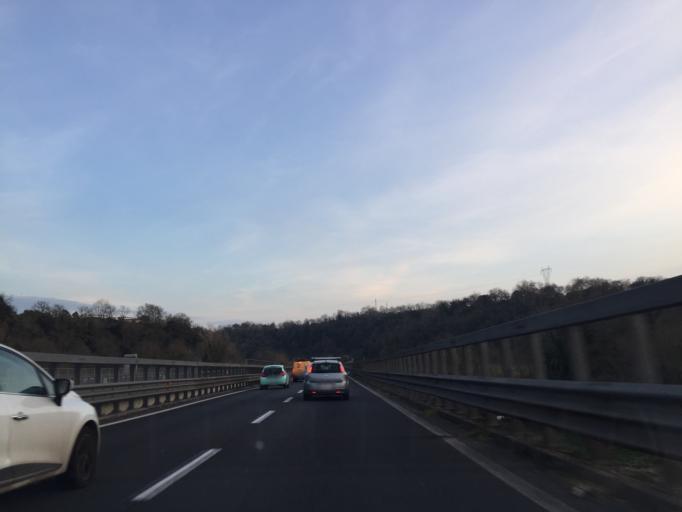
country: IT
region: Latium
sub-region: Citta metropolitana di Roma Capitale
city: Monte Caminetto
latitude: 42.0105
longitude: 12.4379
